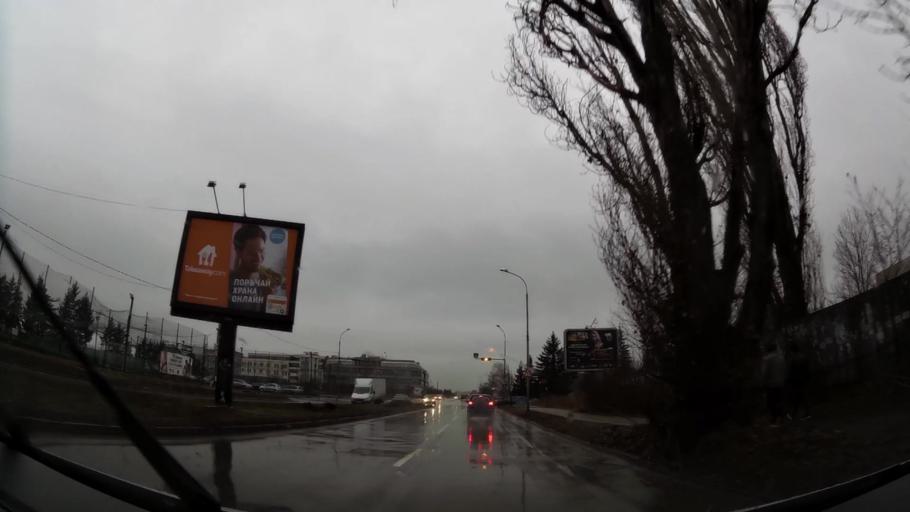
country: BG
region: Sofia-Capital
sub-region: Stolichna Obshtina
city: Sofia
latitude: 42.6517
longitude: 23.3542
